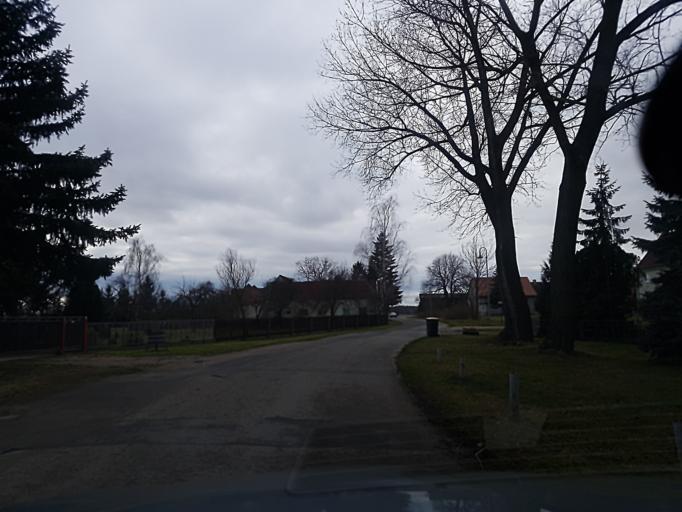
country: DE
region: Brandenburg
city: Falkenberg
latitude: 51.5268
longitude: 13.2942
